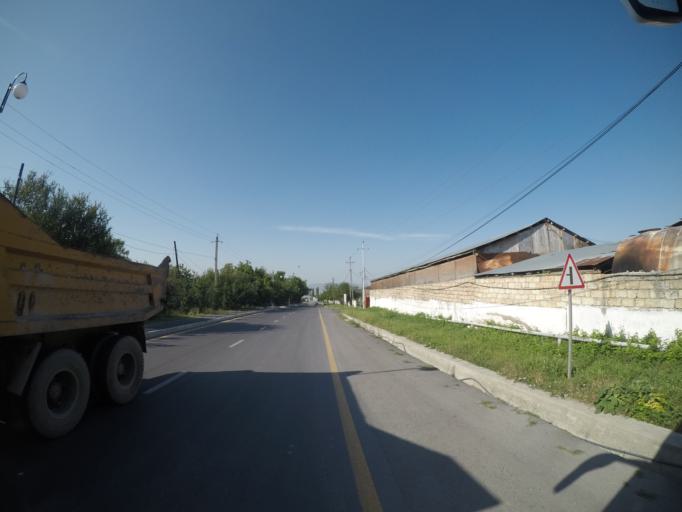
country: AZ
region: Shaki City
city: Sheki
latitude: 41.2153
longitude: 47.1682
